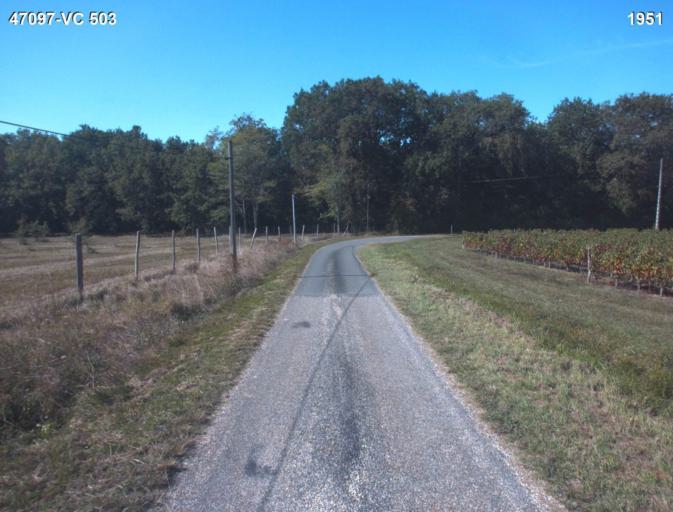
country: FR
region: Aquitaine
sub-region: Departement du Lot-et-Garonne
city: Port-Sainte-Marie
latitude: 44.2080
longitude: 0.3696
